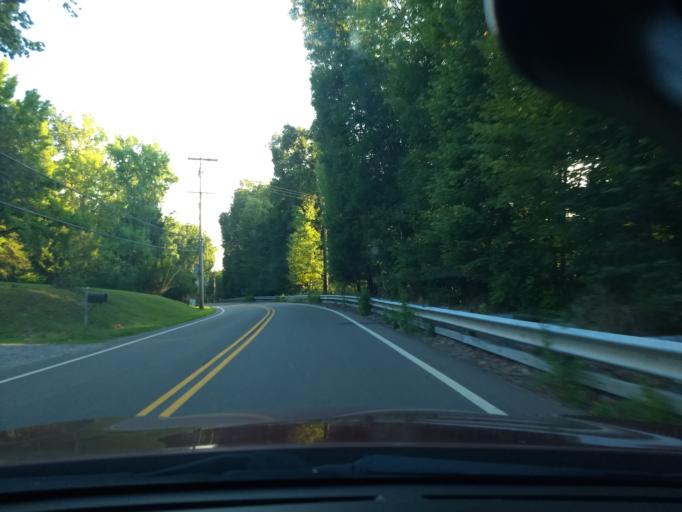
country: US
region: Pennsylvania
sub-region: Allegheny County
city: Bell Acres
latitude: 40.5896
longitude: -80.1492
